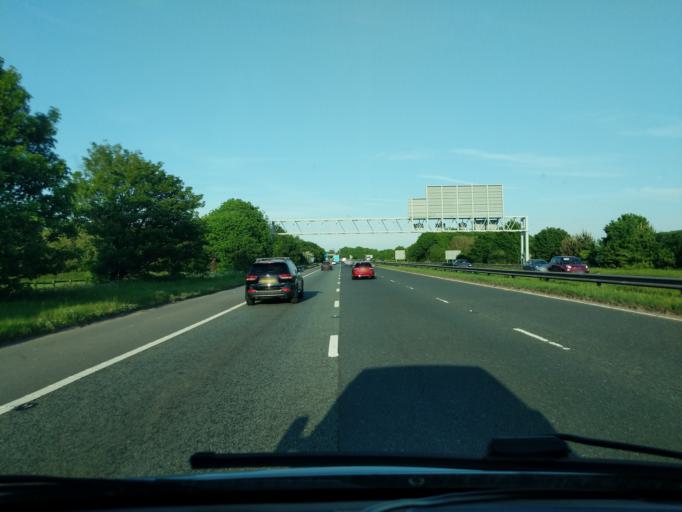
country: GB
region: England
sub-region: Knowsley
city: Whiston
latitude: 53.4010
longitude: -2.7785
